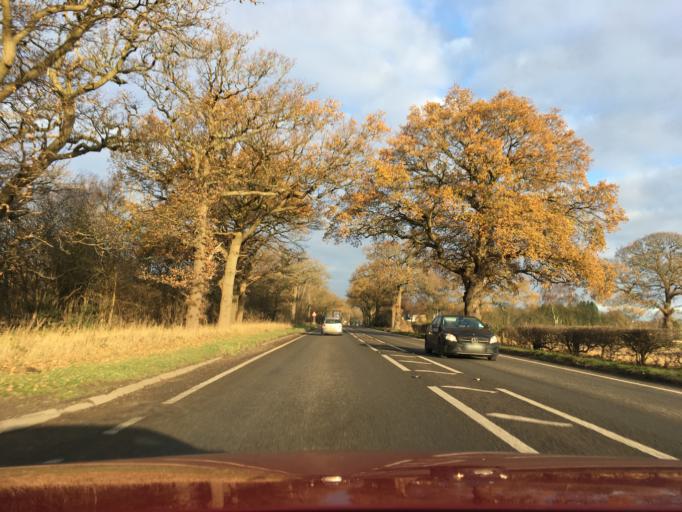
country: GB
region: England
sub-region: City and Borough of Birmingham
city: Sutton Coldfield
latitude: 52.5841
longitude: -1.7790
